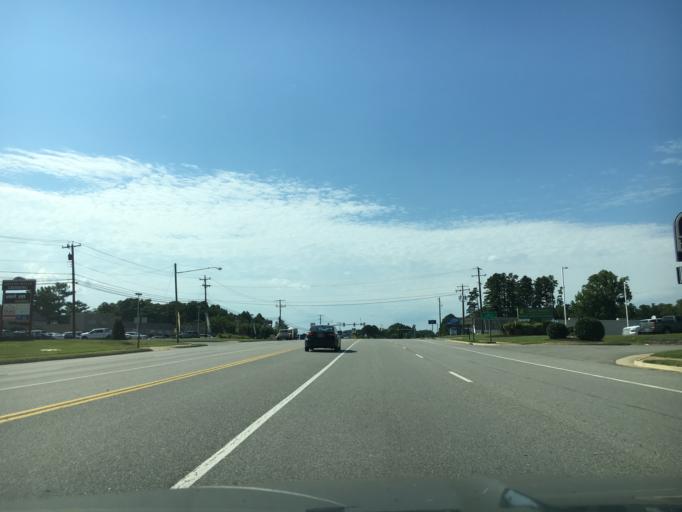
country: US
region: Virginia
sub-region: Halifax County
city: Halifax
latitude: 36.7397
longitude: -78.9214
